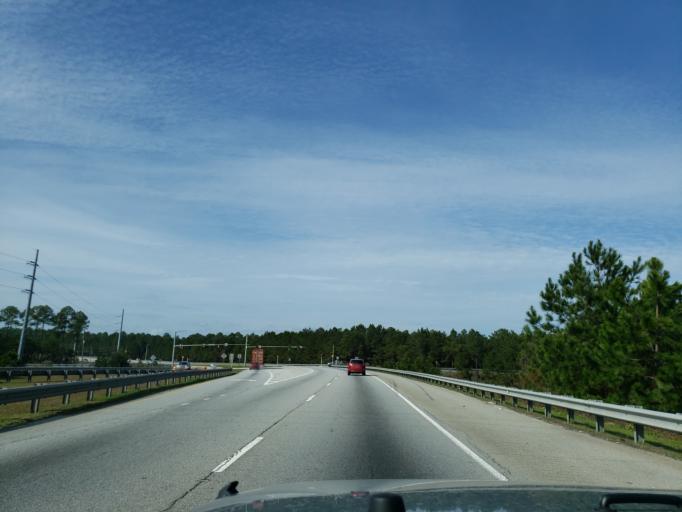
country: US
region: Georgia
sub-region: Chatham County
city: Port Wentworth
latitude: 32.1669
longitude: -81.2162
